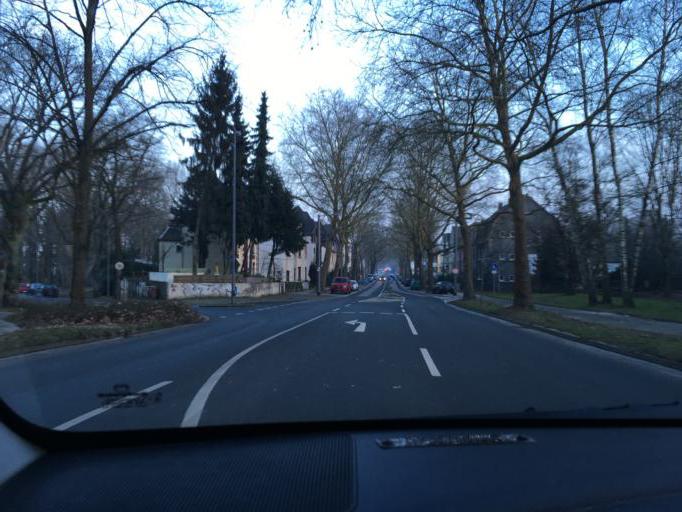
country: DE
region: North Rhine-Westphalia
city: Witten
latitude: 51.4628
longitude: 7.3201
